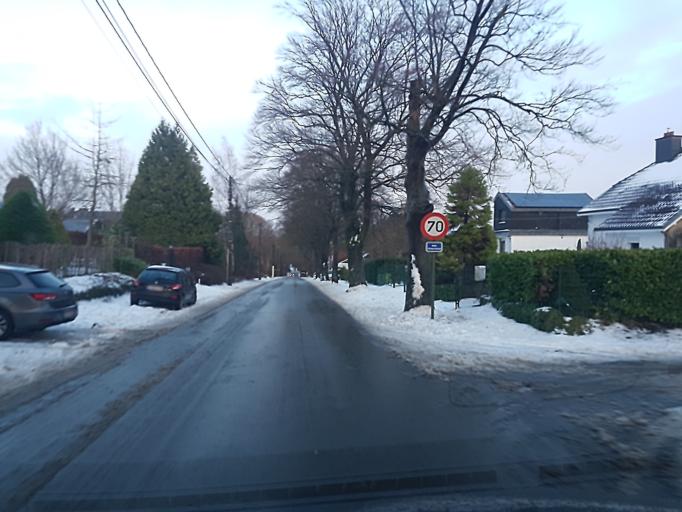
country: BE
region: Wallonia
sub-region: Province de Liege
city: Spa
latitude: 50.4779
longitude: 5.8507
